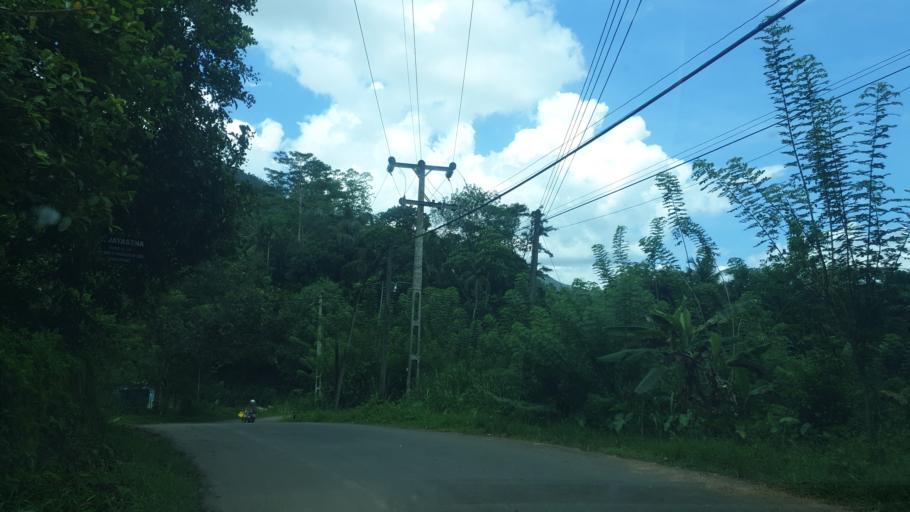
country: LK
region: Sabaragamuwa
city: Ratnapura
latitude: 6.4805
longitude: 80.4136
